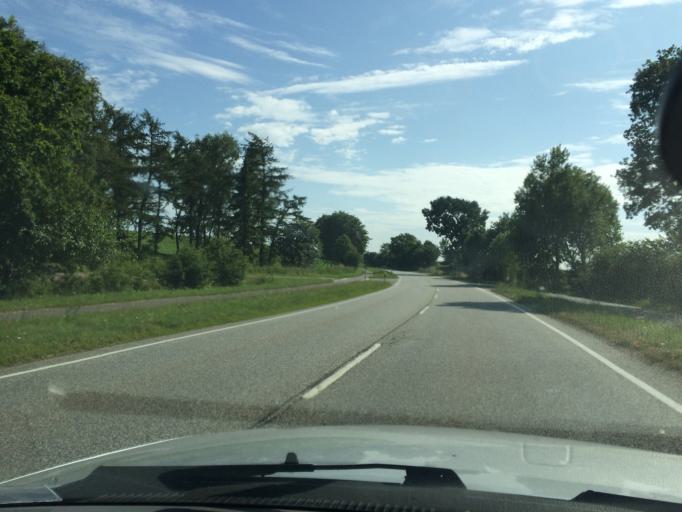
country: DE
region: Schleswig-Holstein
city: Oeversee
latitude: 54.7134
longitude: 9.4406
